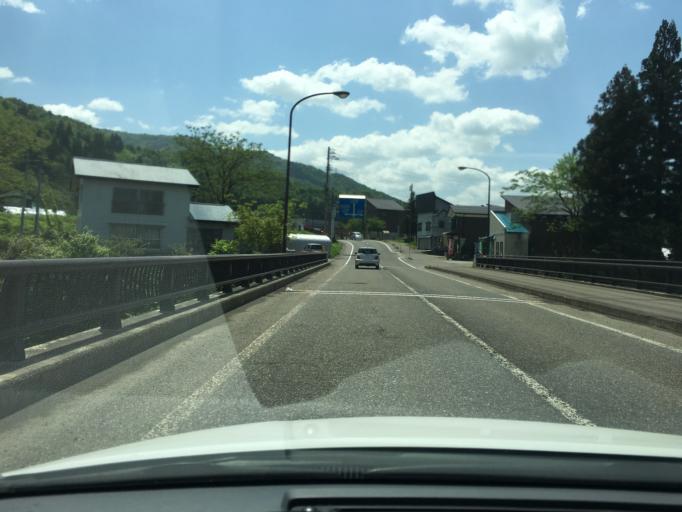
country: JP
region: Niigata
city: Tochio-honcho
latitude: 37.3489
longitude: 139.0492
